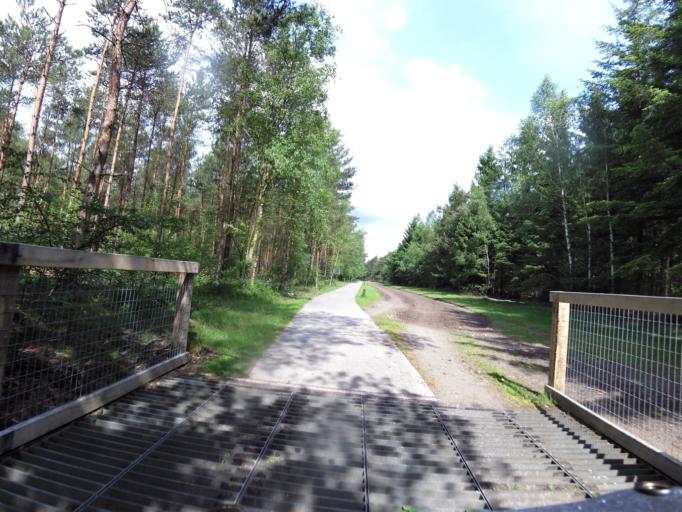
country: NL
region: Gelderland
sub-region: Gemeente Apeldoorn
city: Uddel
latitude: 52.3031
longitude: 5.7775
